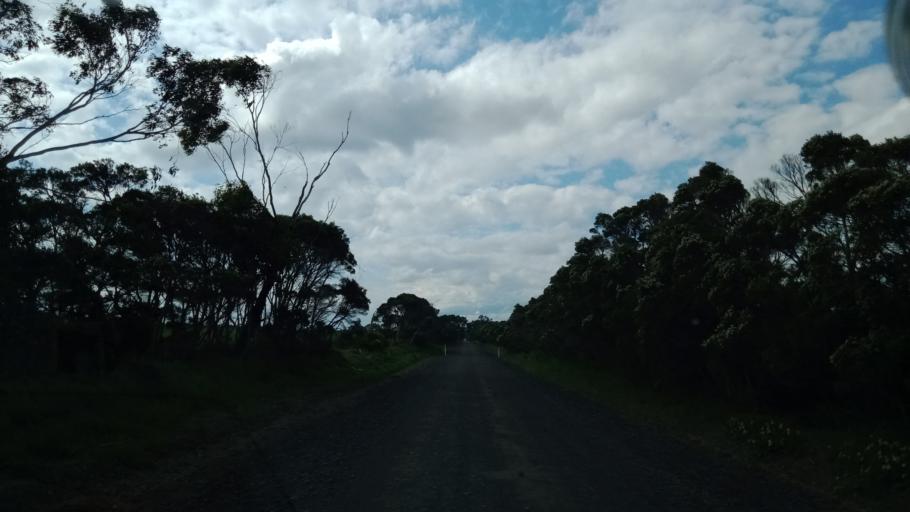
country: AU
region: Victoria
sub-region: Frankston
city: Skye
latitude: -38.1002
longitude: 145.2162
